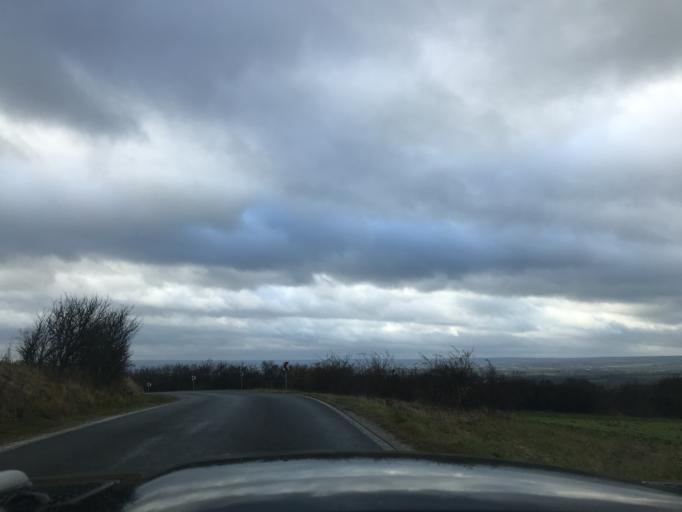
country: DE
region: Thuringia
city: Sollstedt
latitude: 51.2615
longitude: 10.4780
